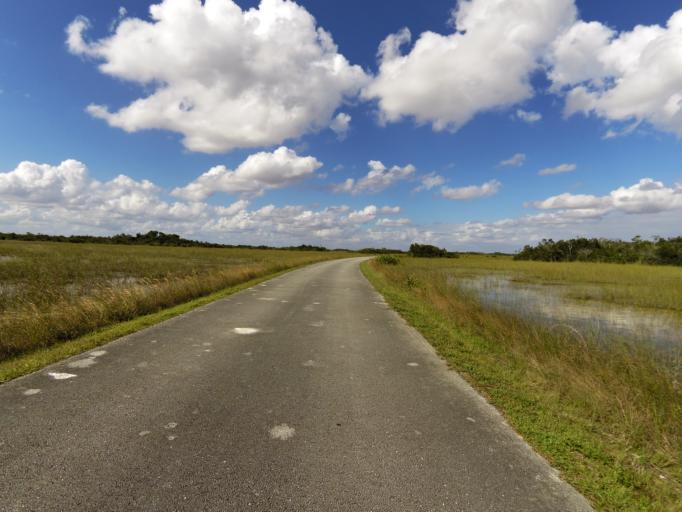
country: US
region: Florida
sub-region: Miami-Dade County
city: The Hammocks
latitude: 25.7105
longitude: -80.7616
